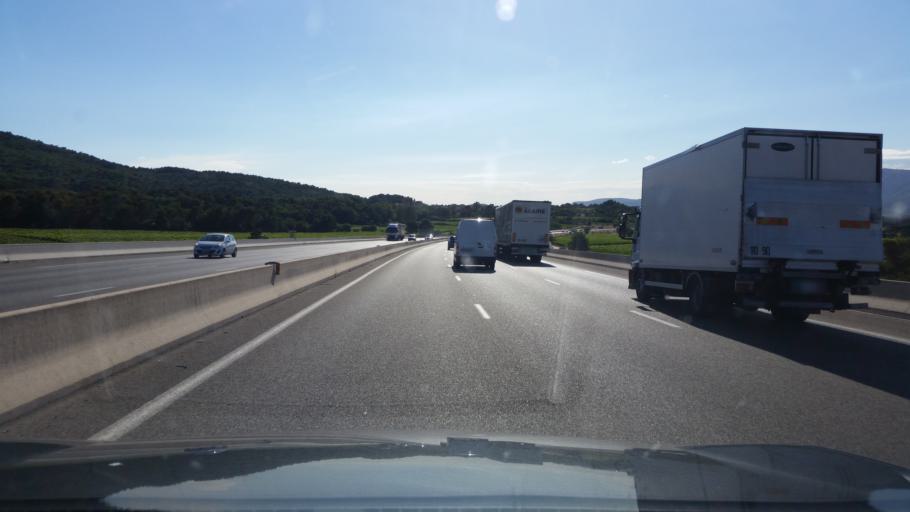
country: FR
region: Provence-Alpes-Cote d'Azur
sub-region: Departement du Var
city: Saint-Maximin-la-Sainte-Baume
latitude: 43.4717
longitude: 5.8005
